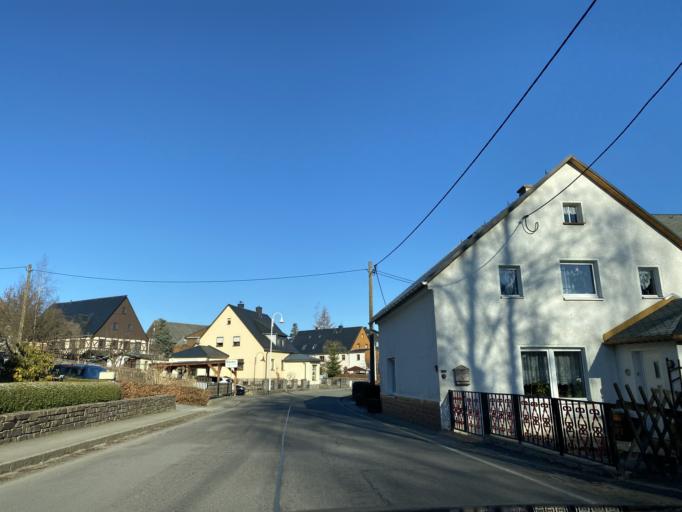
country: DE
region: Saxony
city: Mildenau
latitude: 50.5981
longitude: 13.0681
